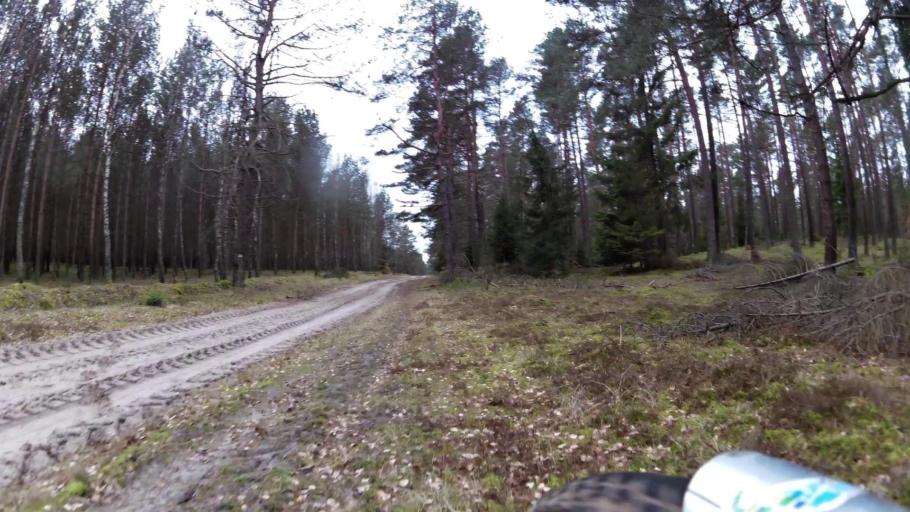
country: PL
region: Pomeranian Voivodeship
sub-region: Powiat bytowski
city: Trzebielino
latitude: 54.1254
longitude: 17.1327
